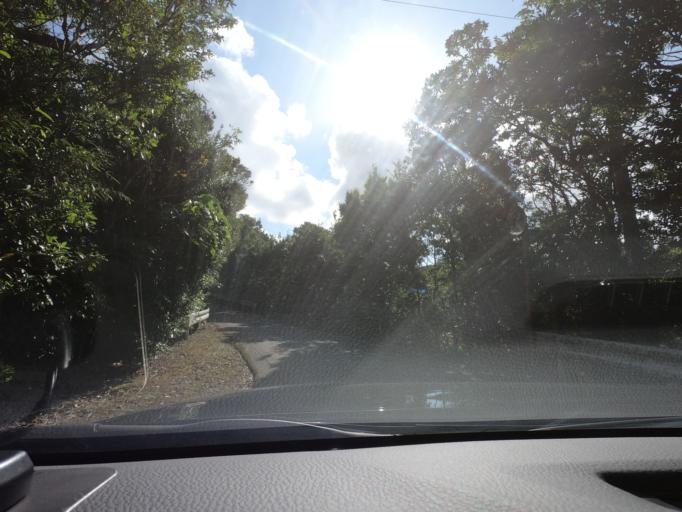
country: JP
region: Okinawa
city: Nago
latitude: 26.7551
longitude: 128.2033
